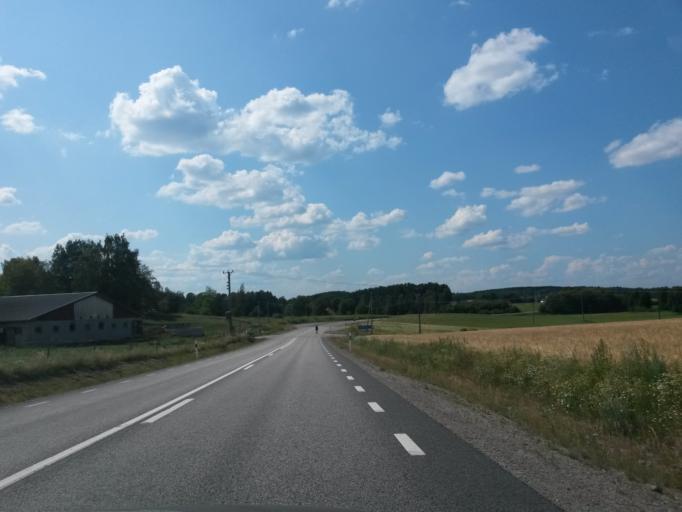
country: SE
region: Vaestra Goetaland
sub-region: Vargarda Kommun
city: Vargarda
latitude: 58.0478
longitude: 12.8332
